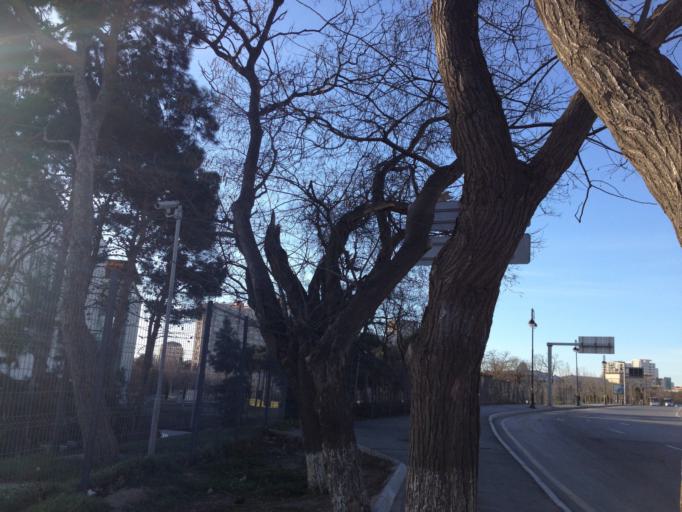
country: AZ
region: Baki
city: Baku
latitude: 40.3954
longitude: 49.8484
